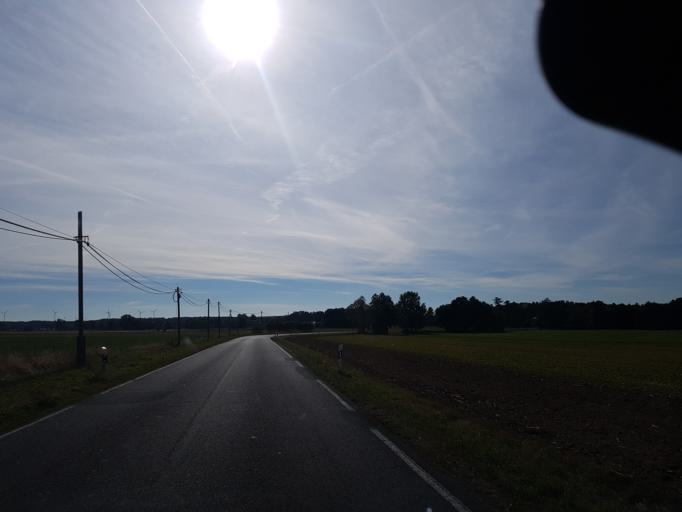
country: DE
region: Brandenburg
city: Schlieben
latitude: 51.7107
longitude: 13.4105
